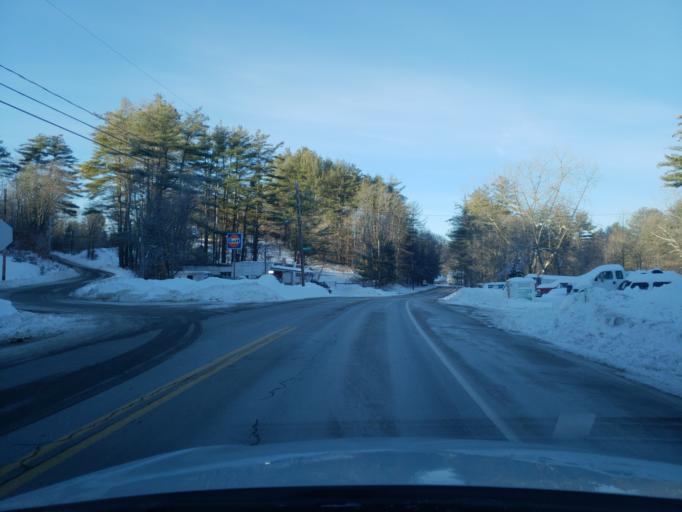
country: US
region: New Hampshire
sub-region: Hillsborough County
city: New Boston
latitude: 42.9809
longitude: -71.6836
